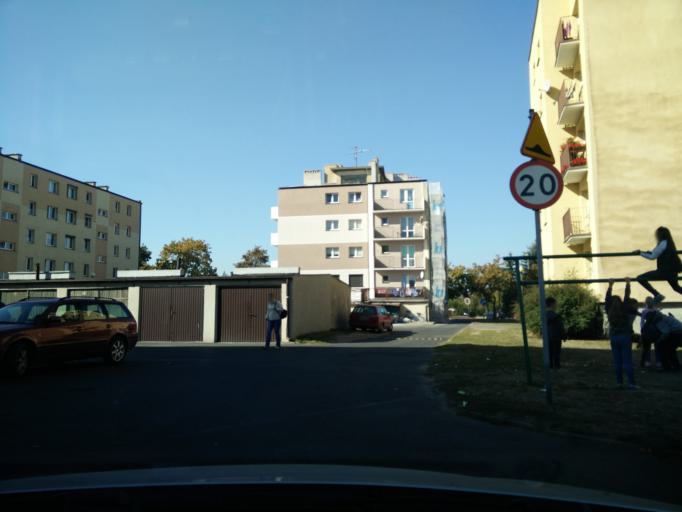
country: PL
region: Greater Poland Voivodeship
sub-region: Powiat sredzki
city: Sroda Wielkopolska
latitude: 52.2308
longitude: 17.2669
